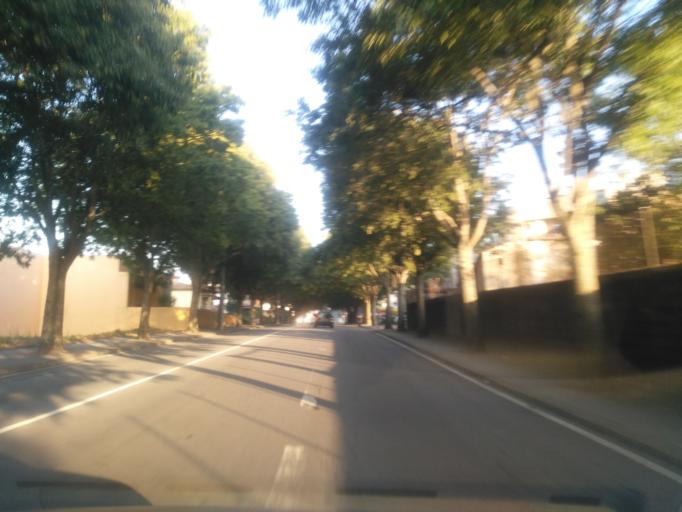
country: PT
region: Braga
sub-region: Braga
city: Braga
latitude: 41.5588
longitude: -8.4439
